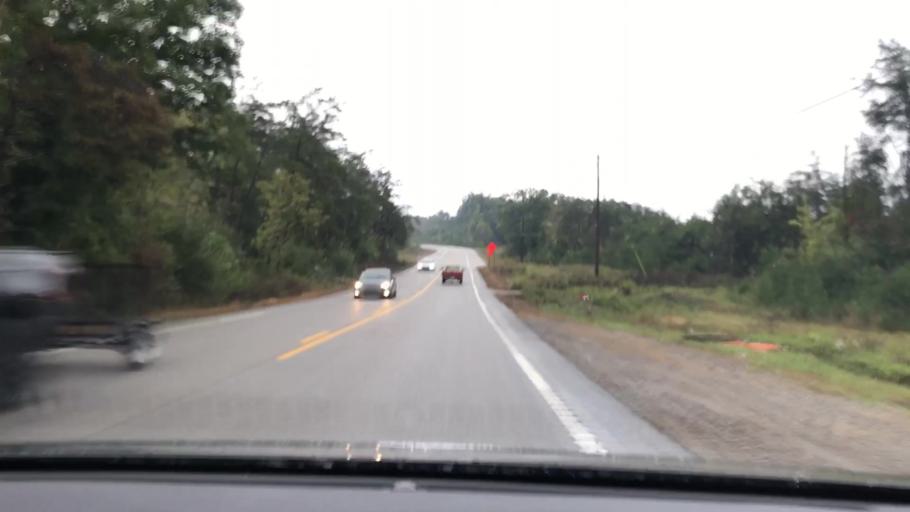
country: US
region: Tennessee
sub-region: Putnam County
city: Monterey
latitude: 36.1187
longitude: -85.1897
